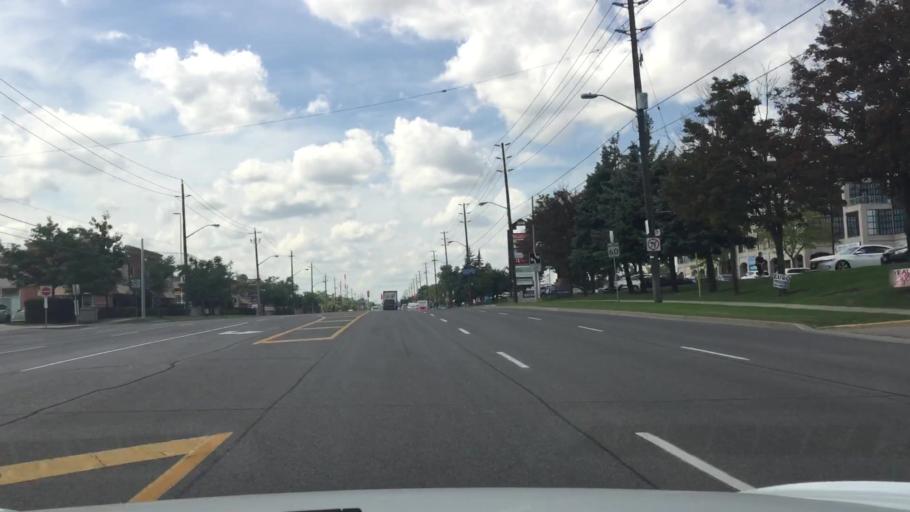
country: CA
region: Ontario
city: Concord
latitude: 43.7869
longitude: -79.4718
